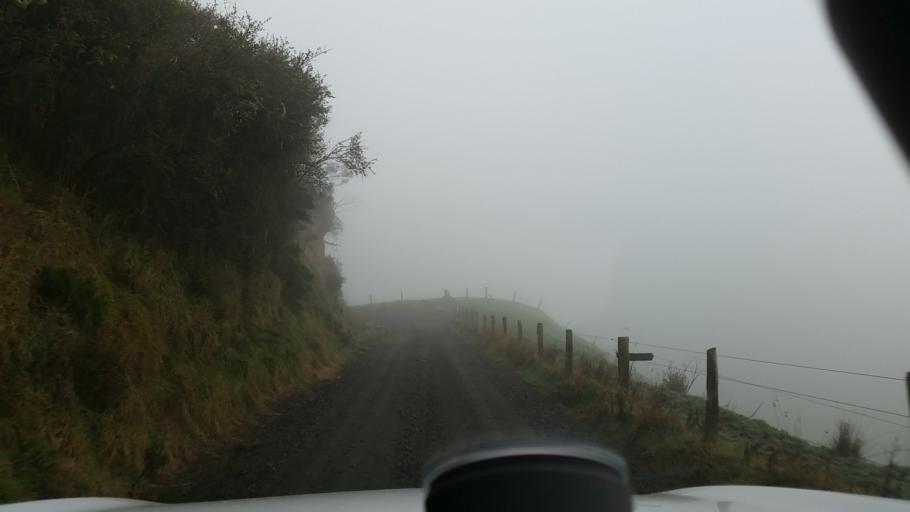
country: NZ
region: Taranaki
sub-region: South Taranaki District
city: Eltham
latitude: -39.4100
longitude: 174.4311
